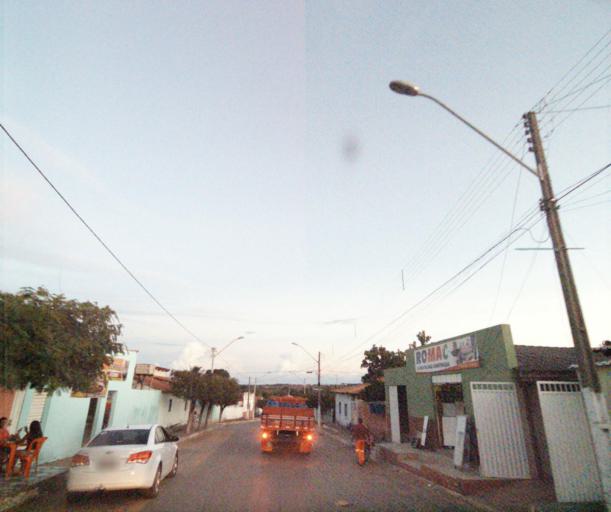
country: BR
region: Bahia
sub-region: Sao Felix Do Coribe
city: Santa Maria da Vitoria
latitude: -13.8294
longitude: -44.4558
